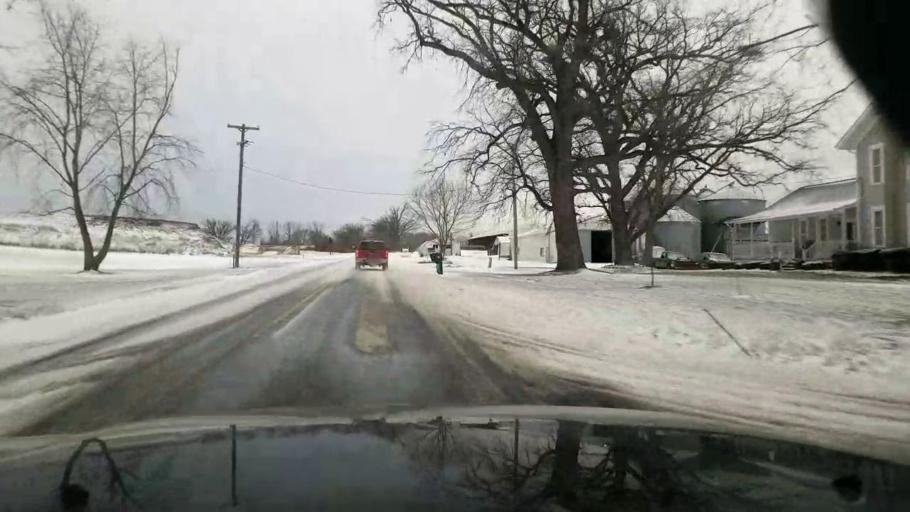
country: US
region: Michigan
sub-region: Jackson County
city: Spring Arbor
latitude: 42.1674
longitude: -84.5003
